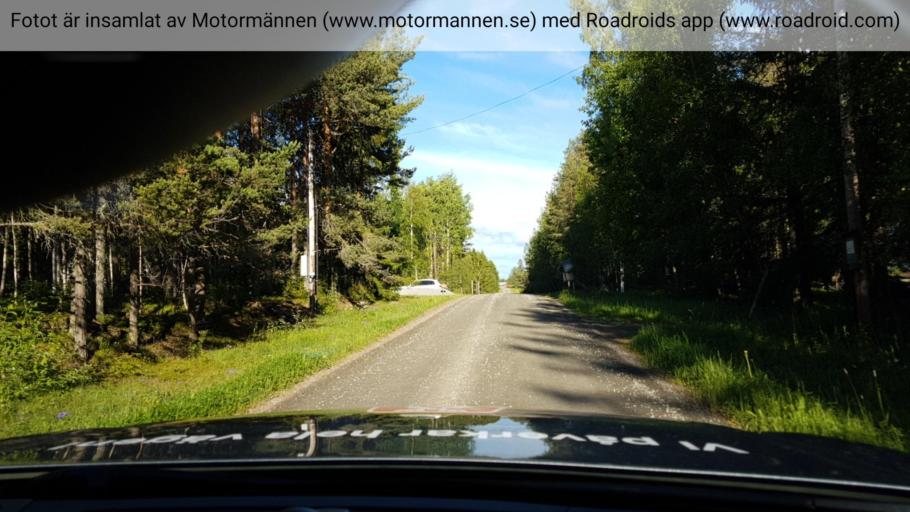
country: SE
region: Jaemtland
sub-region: Bergs Kommun
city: Hoverberg
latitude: 62.9368
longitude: 14.4126
